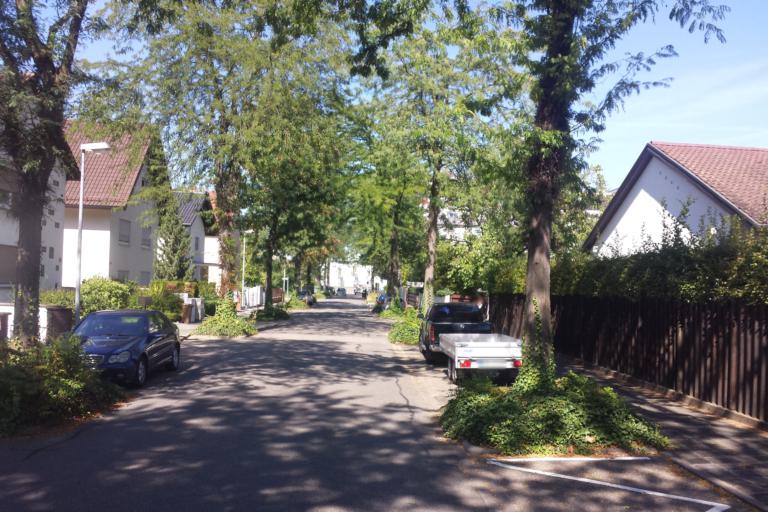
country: DE
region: Hesse
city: Viernheim
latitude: 49.5420
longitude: 8.5881
